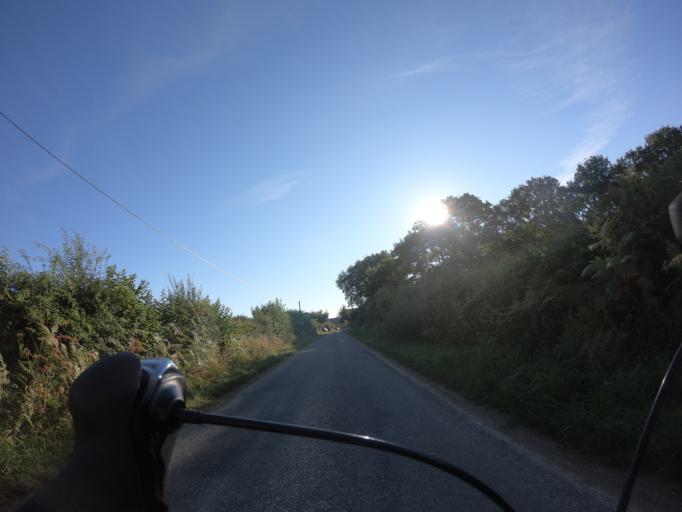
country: FR
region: Lower Normandy
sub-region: Departement de l'Orne
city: Magny-le-Desert
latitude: 48.5351
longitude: -0.2556
